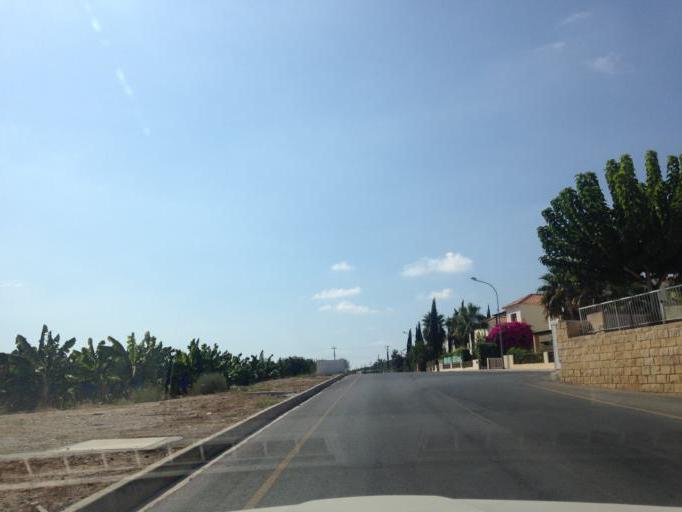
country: CY
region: Pafos
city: Pegeia
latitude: 34.8762
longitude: 32.3677
